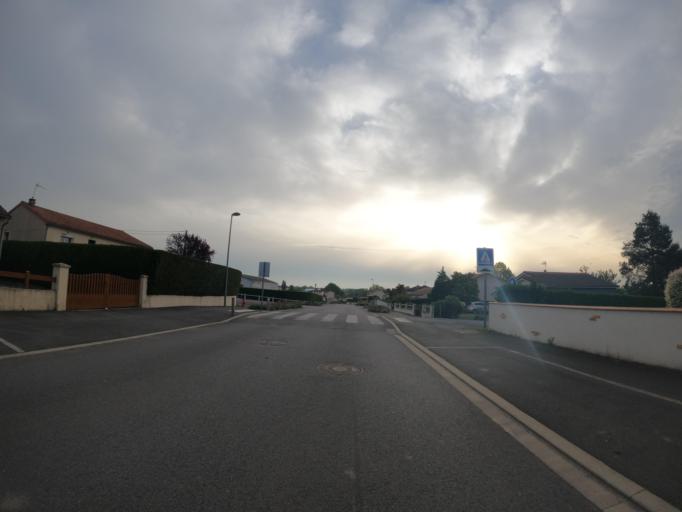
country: FR
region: Poitou-Charentes
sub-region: Departement des Deux-Sevres
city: La Chapelle-Saint-Laurent
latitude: 46.6905
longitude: -0.5036
